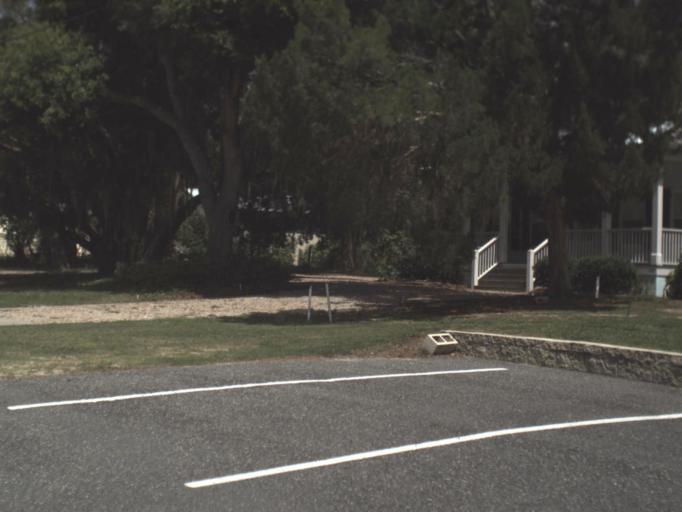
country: US
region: Florida
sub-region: Taylor County
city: Steinhatchee
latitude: 29.6704
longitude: -83.3834
